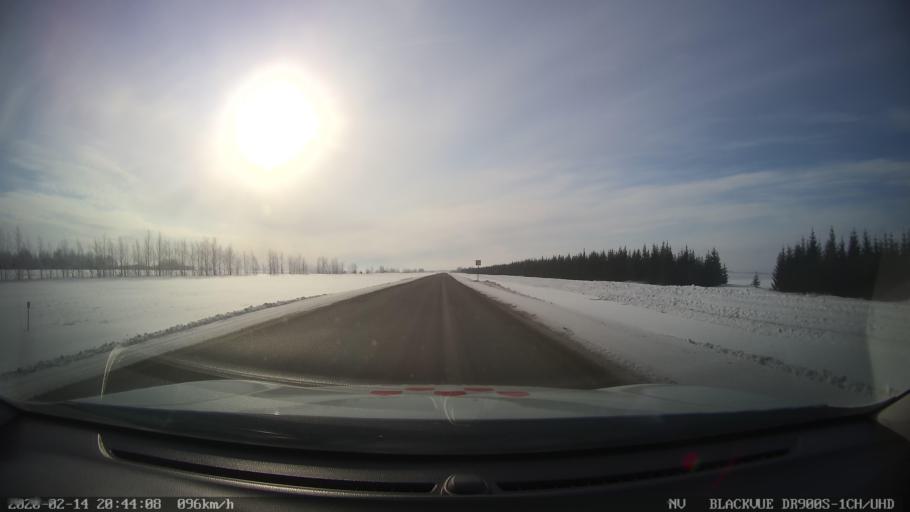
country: RU
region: Tatarstan
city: Kuybyshevskiy Zaton
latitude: 55.2984
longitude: 49.1470
